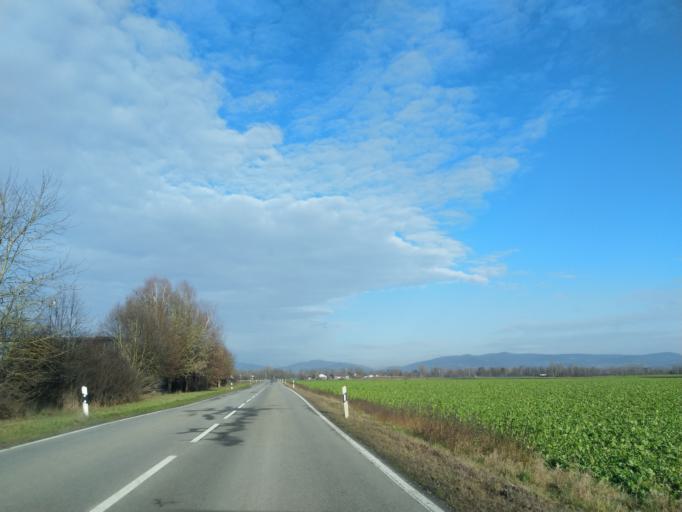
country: DE
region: Bavaria
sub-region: Lower Bavaria
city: Aholming
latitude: 48.7477
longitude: 12.9049
